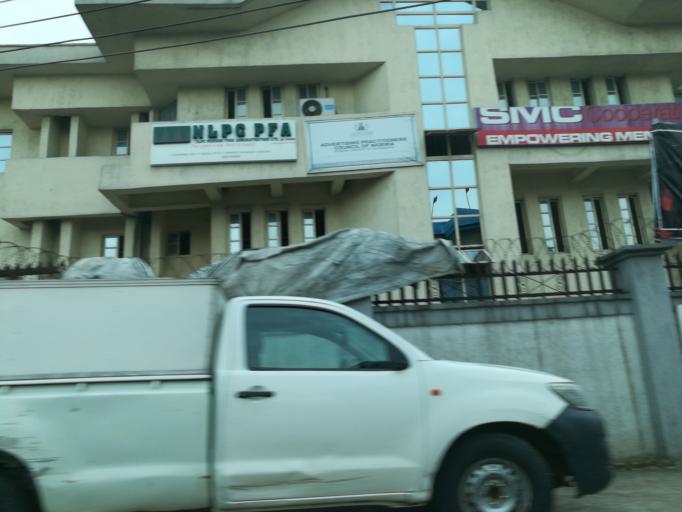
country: NG
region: Rivers
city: Port Harcourt
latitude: 4.8348
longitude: 7.0182
